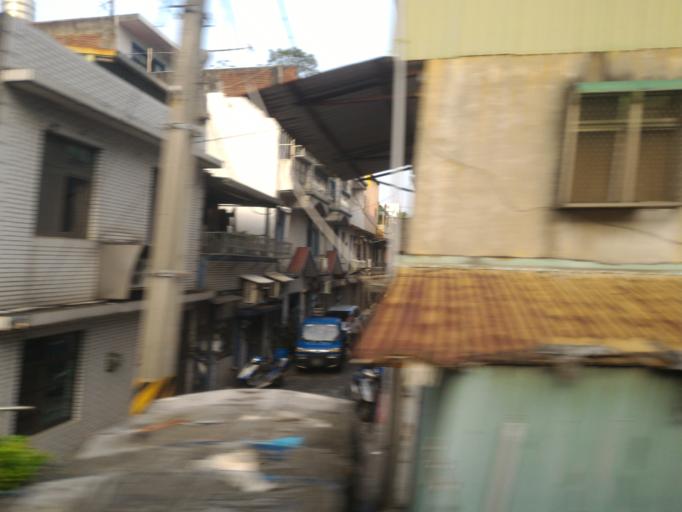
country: TW
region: Taiwan
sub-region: Taoyuan
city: Taoyuan
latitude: 24.9796
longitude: 121.3297
